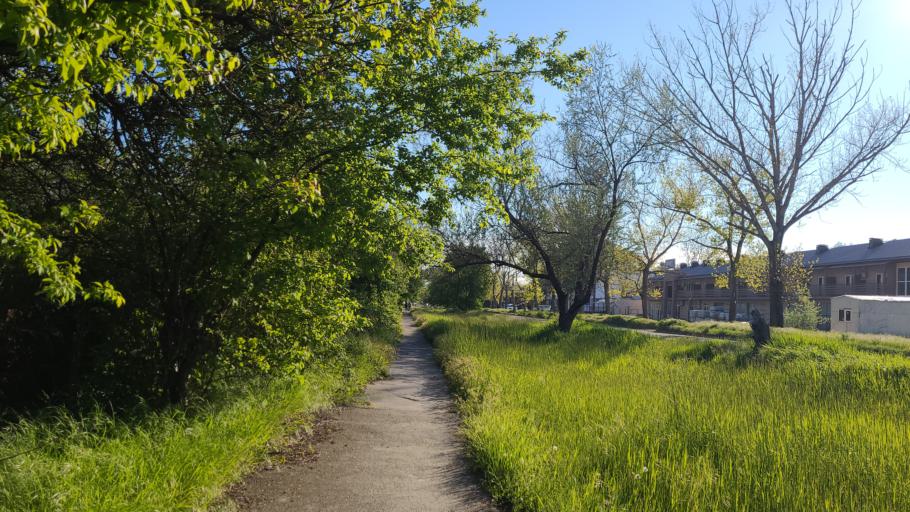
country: RU
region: Krasnodarskiy
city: Tsibanobalka
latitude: 44.9479
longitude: 37.3083
